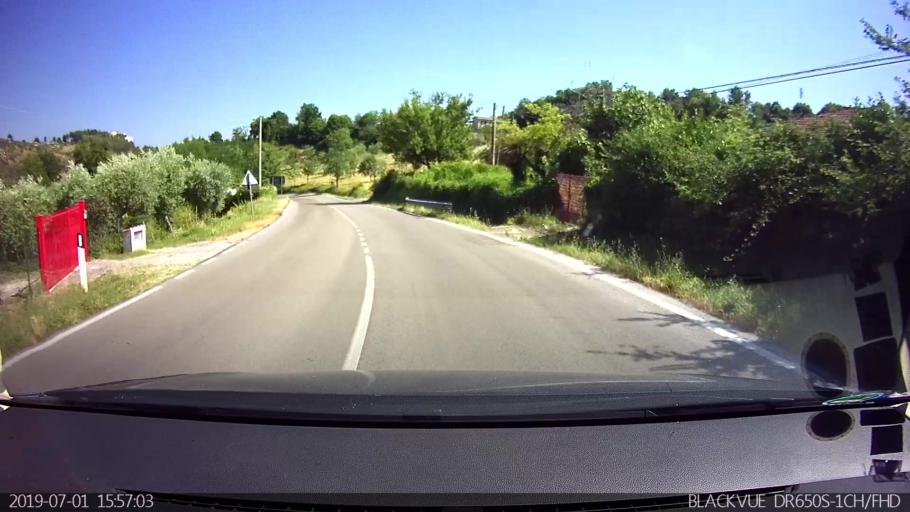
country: IT
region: Latium
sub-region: Provincia di Frosinone
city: Veroli
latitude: 41.6780
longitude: 13.4181
